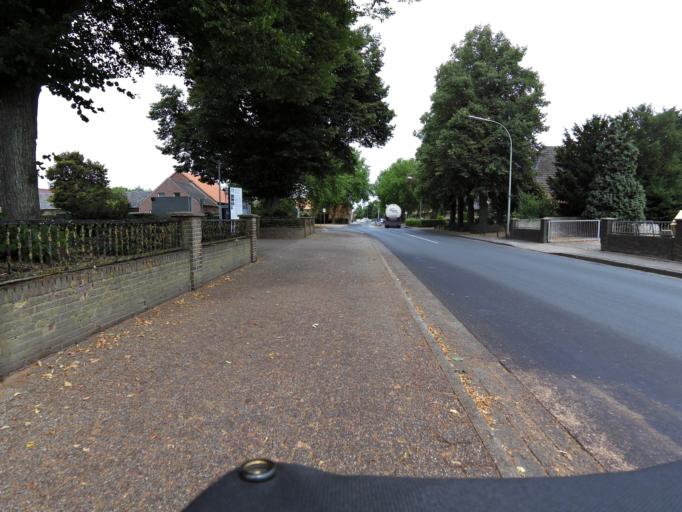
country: DE
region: North Rhine-Westphalia
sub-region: Regierungsbezirk Dusseldorf
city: Weeze
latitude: 51.5861
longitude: 6.1768
